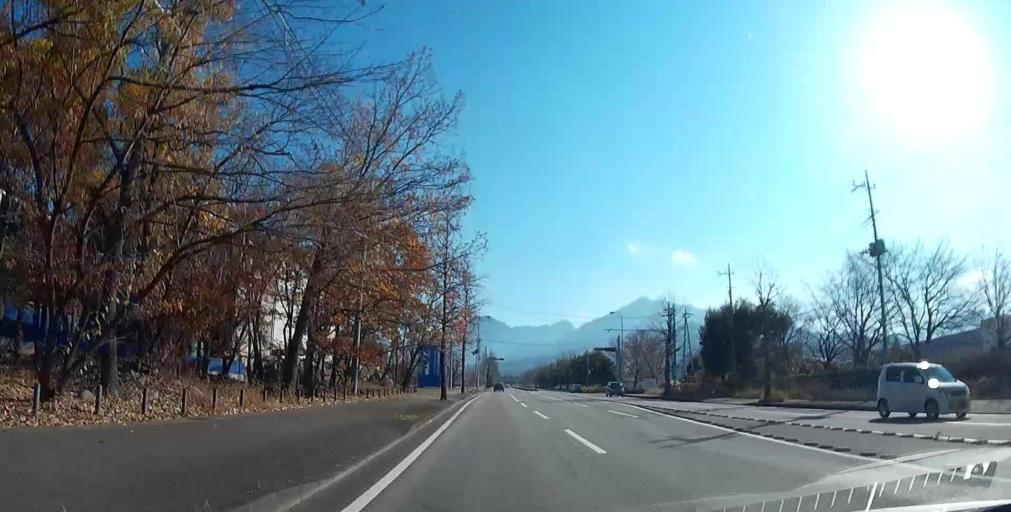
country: JP
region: Yamanashi
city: Isawa
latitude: 35.6276
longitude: 138.6840
